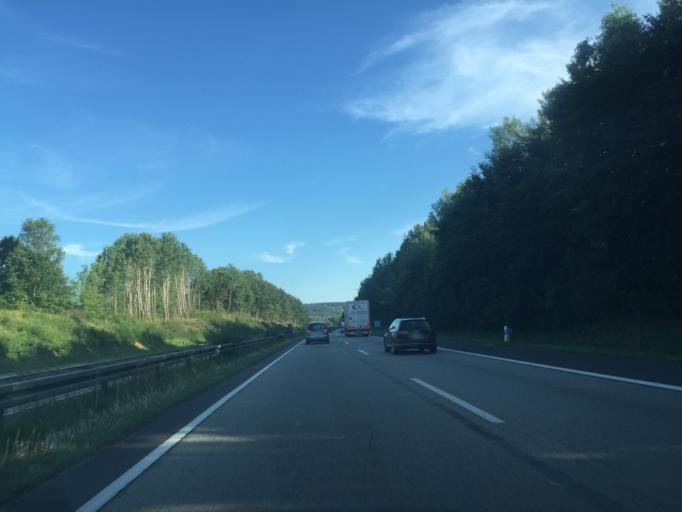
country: DE
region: North Rhine-Westphalia
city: Freudenberg
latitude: 50.9000
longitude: 7.9194
